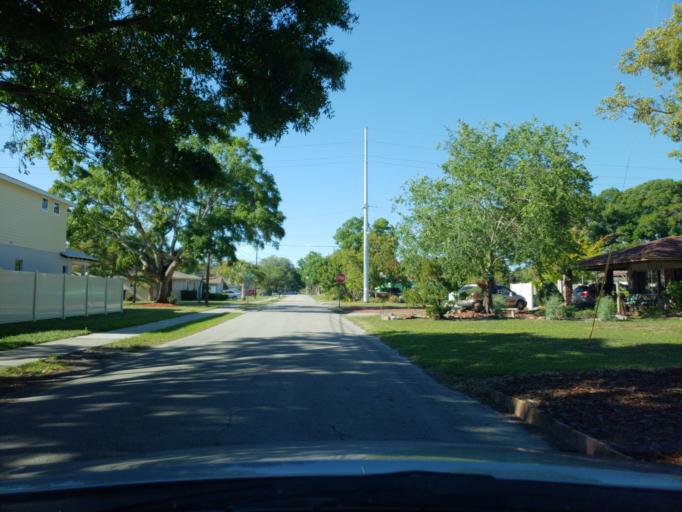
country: US
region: Florida
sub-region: Hillsborough County
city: Tampa
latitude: 27.9505
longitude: -82.4954
